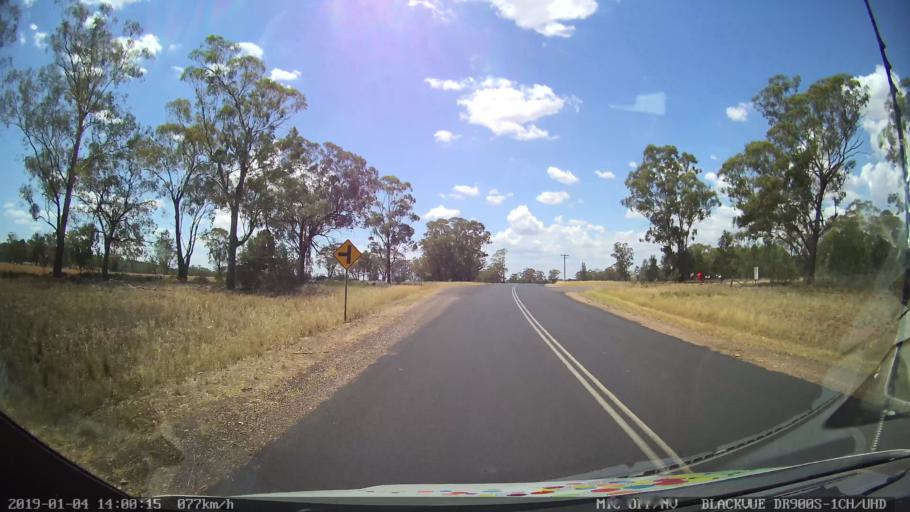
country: AU
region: New South Wales
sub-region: Dubbo Municipality
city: Dubbo
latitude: -32.3081
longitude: 148.5913
